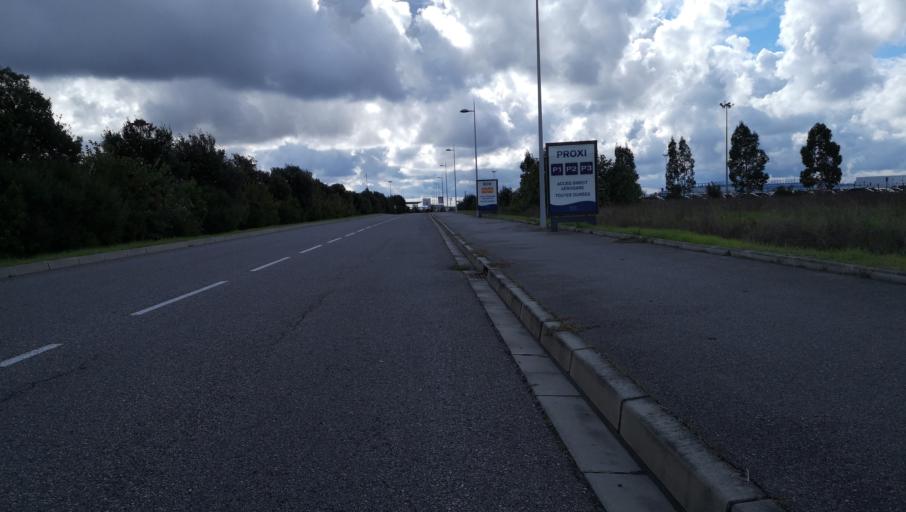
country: FR
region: Midi-Pyrenees
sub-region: Departement de la Haute-Garonne
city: Beauzelle
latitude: 43.6411
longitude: 1.3645
